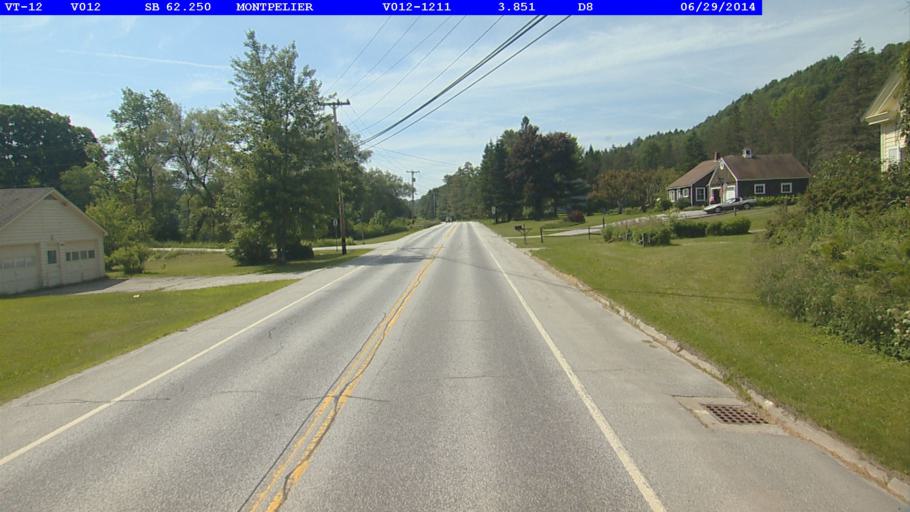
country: US
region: Vermont
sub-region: Washington County
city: Montpelier
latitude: 44.2973
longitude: -72.5797
